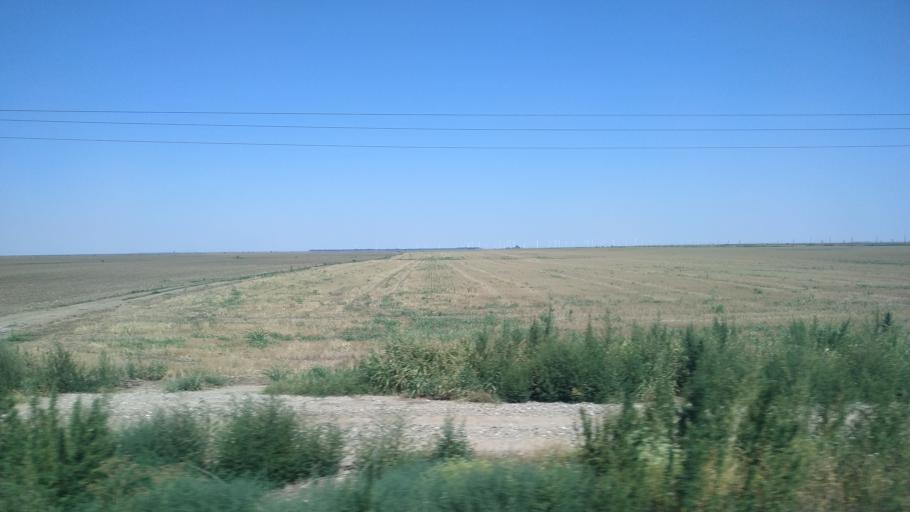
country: RO
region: Calarasi
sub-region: Comuna Borcea
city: Borcea
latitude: 44.4194
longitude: 27.7265
